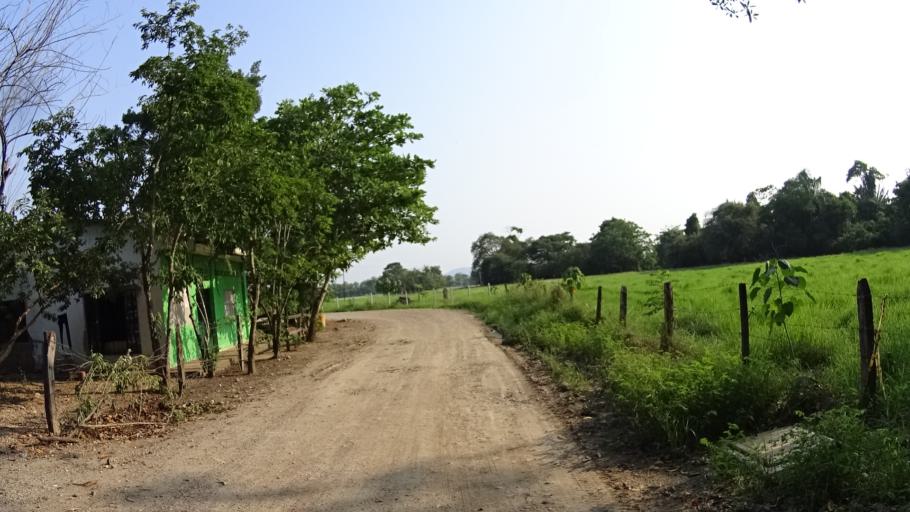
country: CO
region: Cundinamarca
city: Puerto Salgar
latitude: 5.5344
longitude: -74.6850
